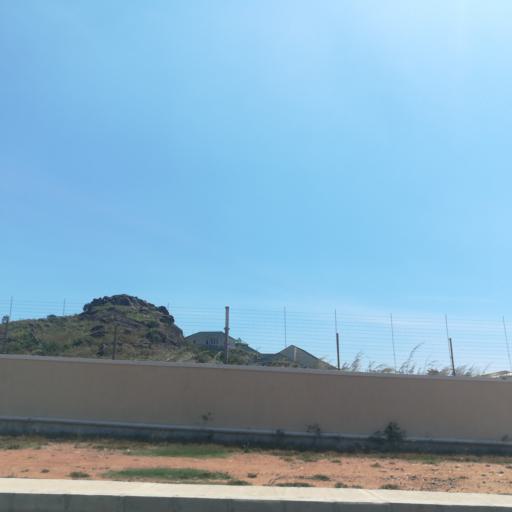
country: NG
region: Plateau
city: Bukuru
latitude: 9.8209
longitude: 8.8787
